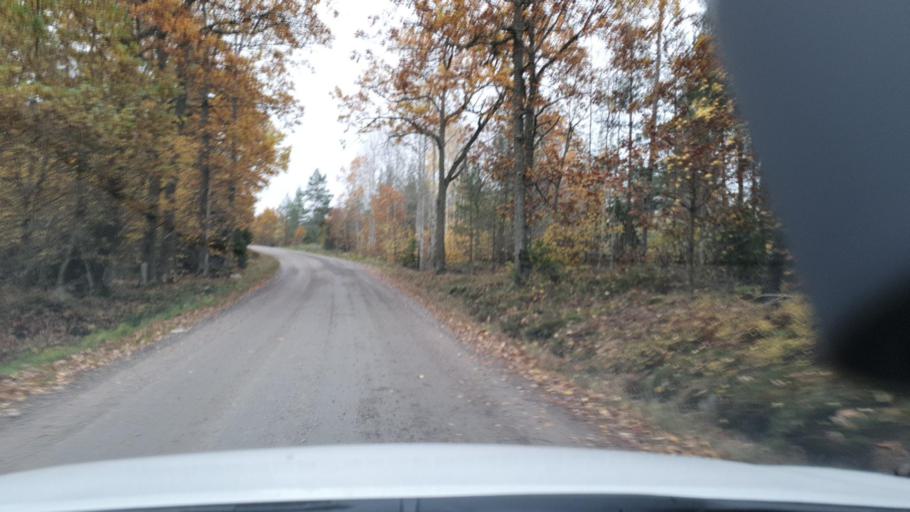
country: SE
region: Kalmar
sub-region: Vasterviks Kommun
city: Ankarsrum
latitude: 57.6994
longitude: 16.4555
